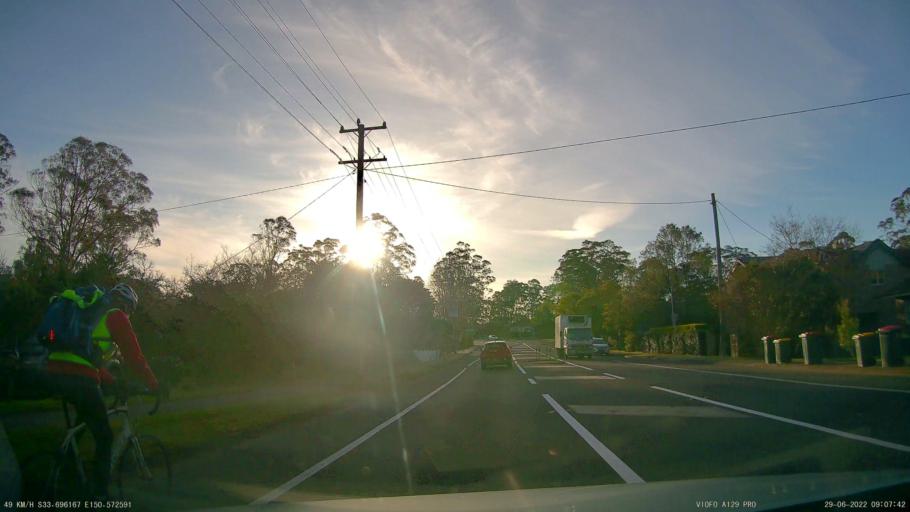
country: AU
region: New South Wales
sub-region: Blue Mountains Municipality
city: Blaxland
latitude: -33.6961
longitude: 150.5730
